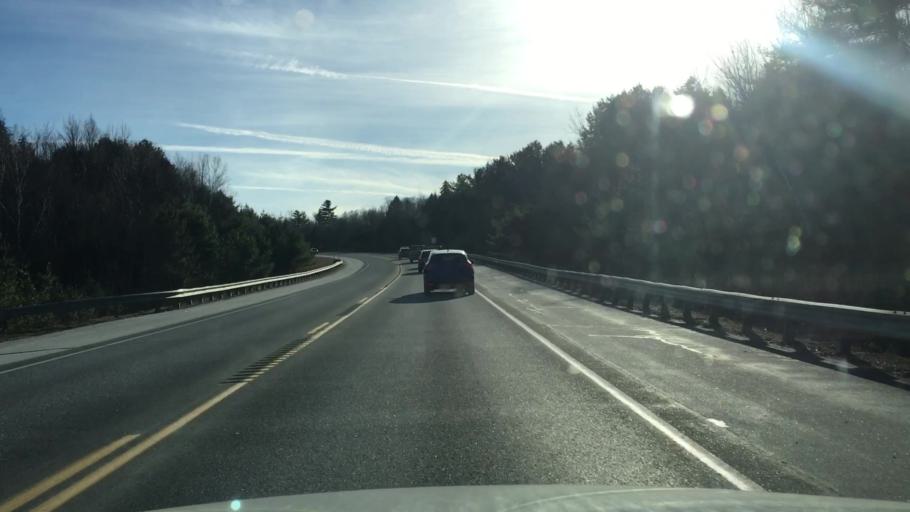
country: US
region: Maine
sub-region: Hancock County
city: Dedham
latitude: 44.6770
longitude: -68.5786
